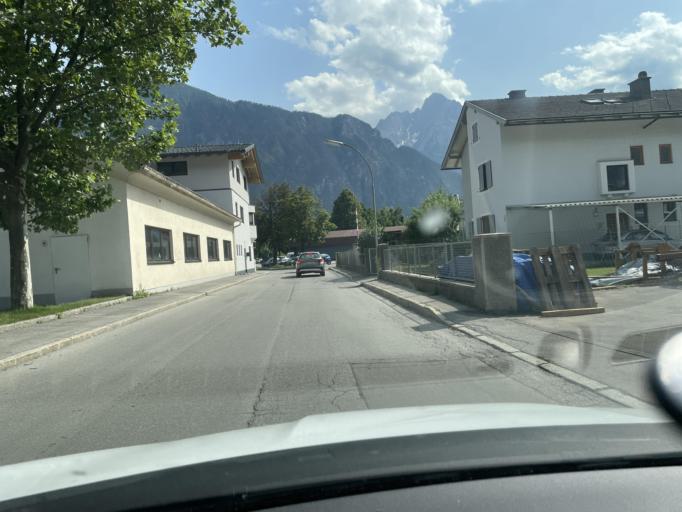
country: AT
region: Tyrol
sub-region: Politischer Bezirk Lienz
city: Lienz
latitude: 46.8319
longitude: 12.7747
